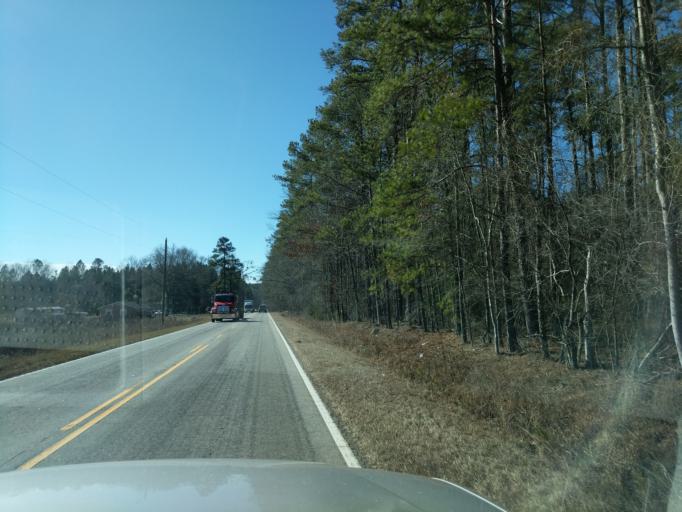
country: US
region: South Carolina
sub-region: Laurens County
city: Joanna
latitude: 34.2612
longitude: -81.8588
